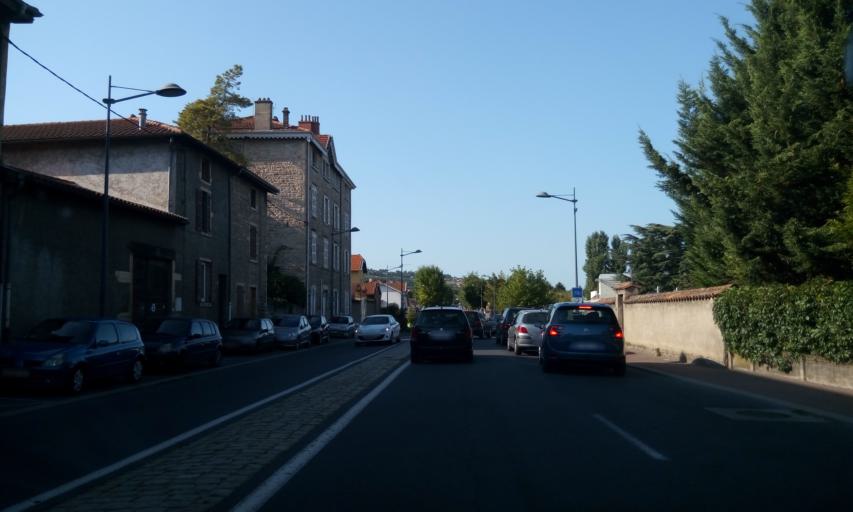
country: FR
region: Rhone-Alpes
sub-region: Departement du Rhone
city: Anse
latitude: 45.9395
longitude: 4.7166
